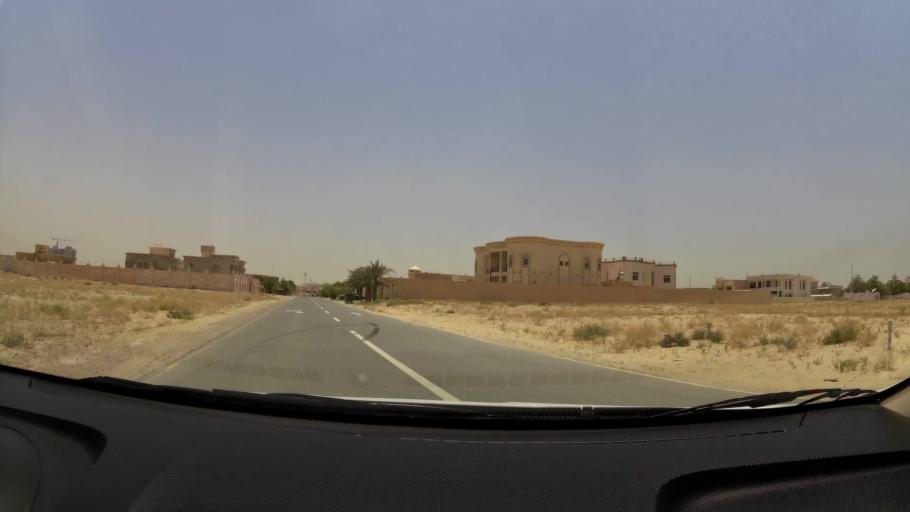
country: AE
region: Ajman
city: Ajman
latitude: 25.4105
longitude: 55.5025
